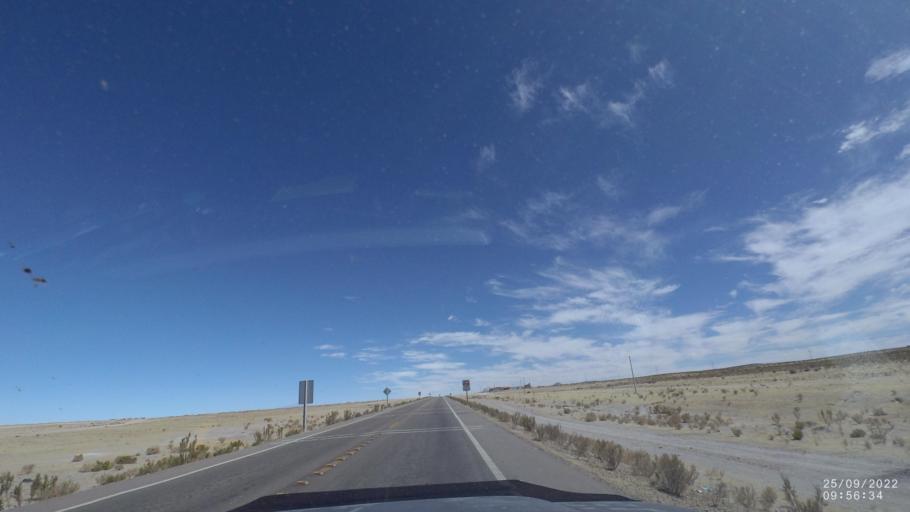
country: BO
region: Potosi
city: Colchani
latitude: -20.3254
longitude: -66.9222
